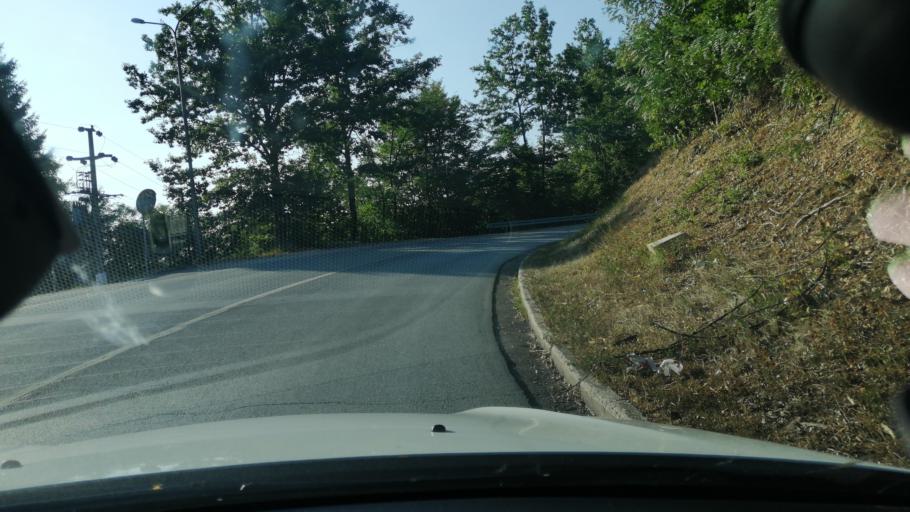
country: RS
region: Central Serbia
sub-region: Moravicki Okrug
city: Ivanjica
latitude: 43.6412
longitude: 20.2375
